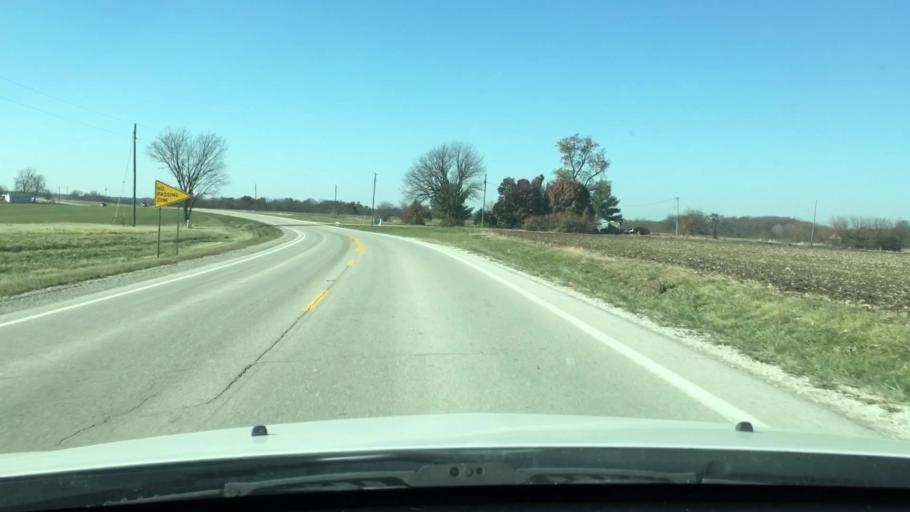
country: US
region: Illinois
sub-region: Pike County
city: Pittsfield
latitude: 39.6195
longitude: -90.7210
